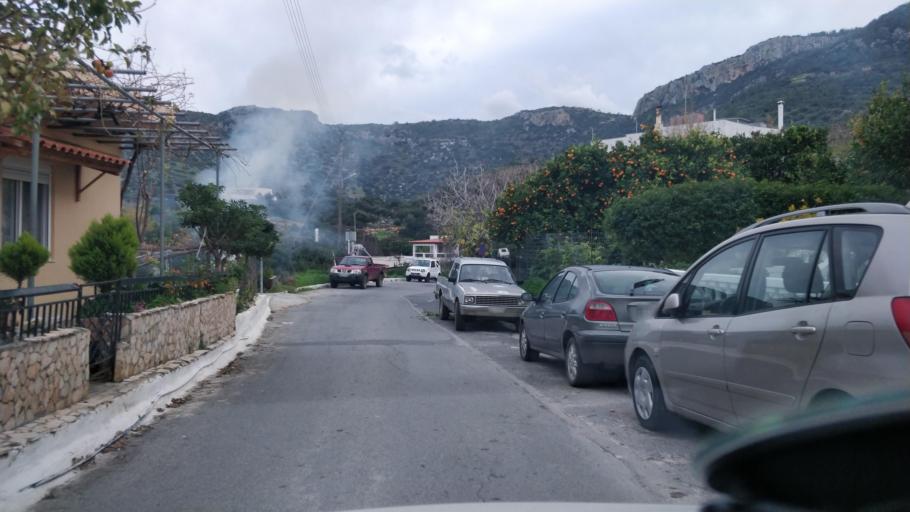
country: GR
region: Crete
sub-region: Nomos Lasithiou
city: Agios Nikolaos
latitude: 35.1153
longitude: 25.7247
